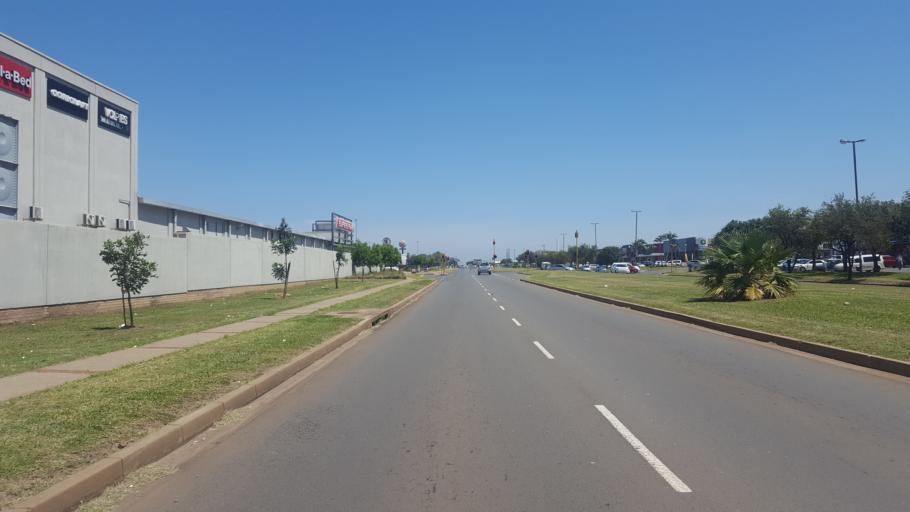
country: ZA
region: KwaZulu-Natal
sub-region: uThungulu District Municipality
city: Richards Bay
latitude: -28.7457
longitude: 32.0507
